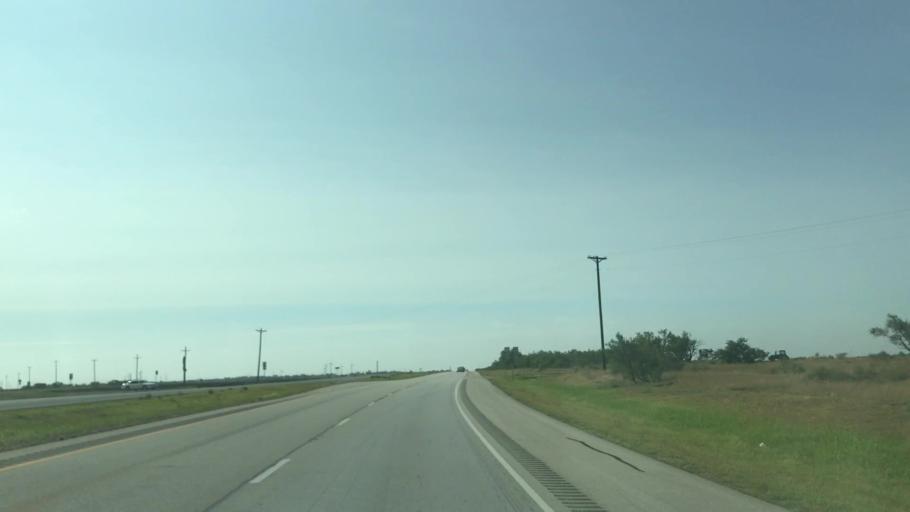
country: US
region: Texas
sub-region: Scurry County
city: Snyder
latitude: 32.6538
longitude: -100.7786
